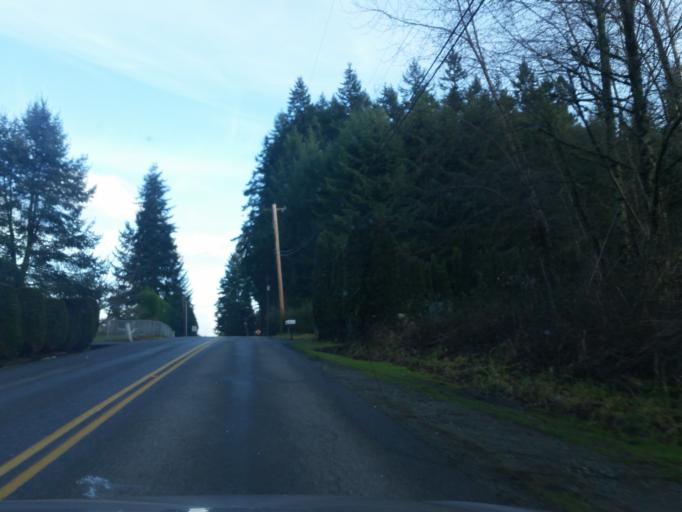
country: US
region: Washington
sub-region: Snohomish County
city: Maltby
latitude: 47.7796
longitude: -122.1355
